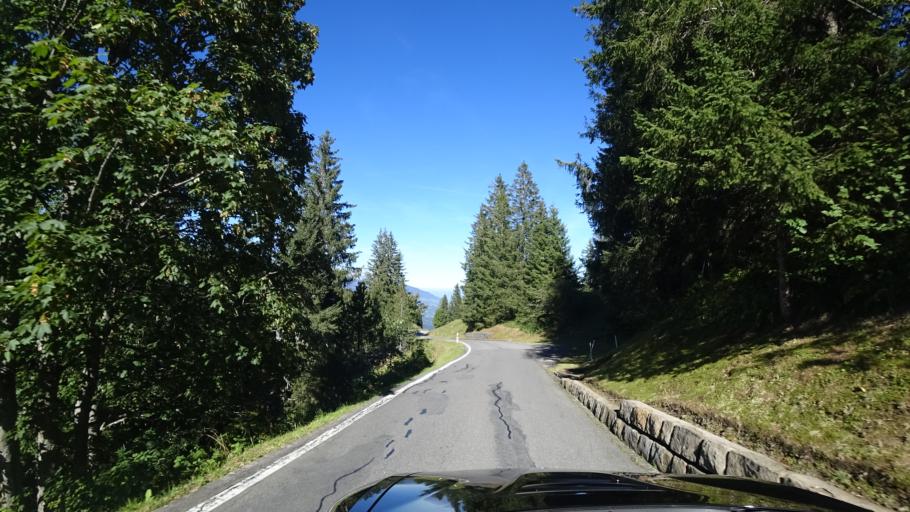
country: CH
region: Obwalden
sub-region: Obwalden
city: Lungern
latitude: 46.8233
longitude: 8.0977
